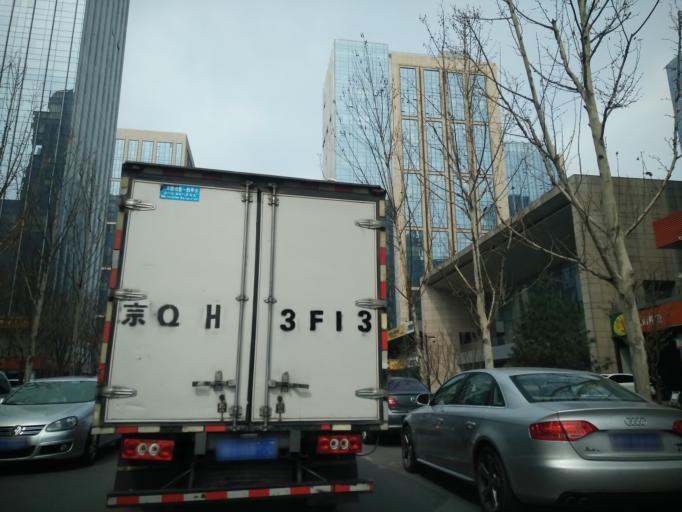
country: CN
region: Beijing
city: Jiugong
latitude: 39.8039
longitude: 116.4884
